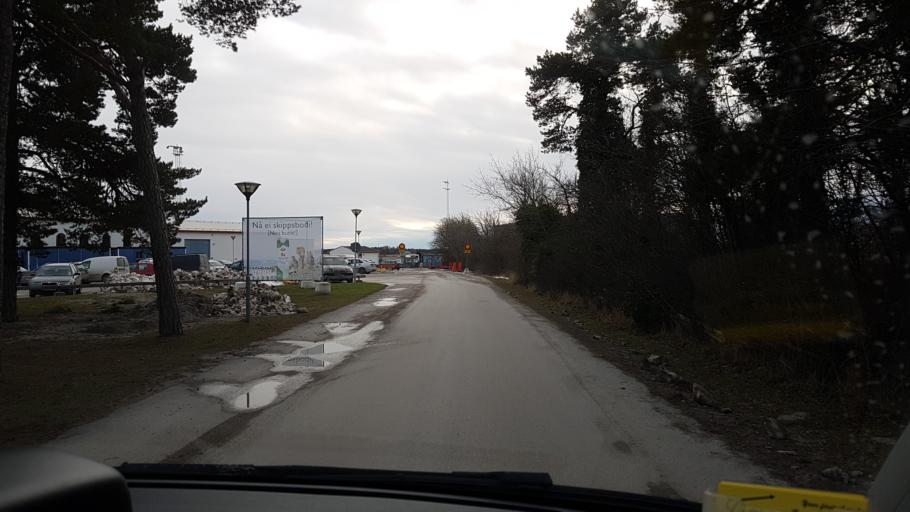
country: SE
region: Gotland
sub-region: Gotland
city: Visby
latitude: 57.6604
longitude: 18.3371
